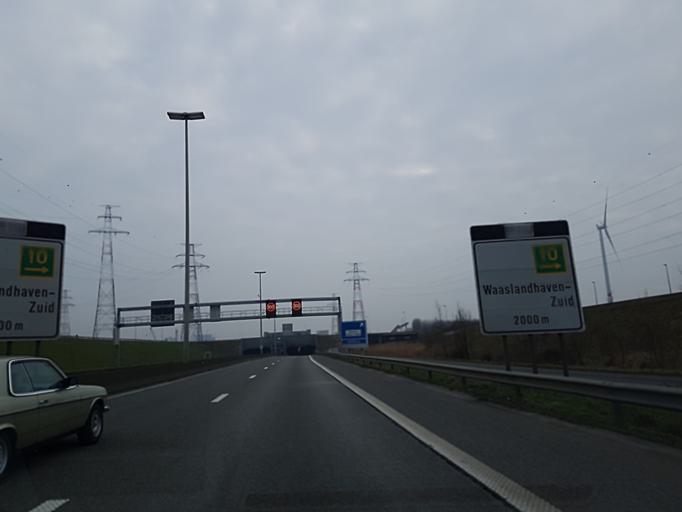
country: BE
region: Flanders
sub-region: Provincie Oost-Vlaanderen
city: Beveren
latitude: 51.2713
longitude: 4.2775
